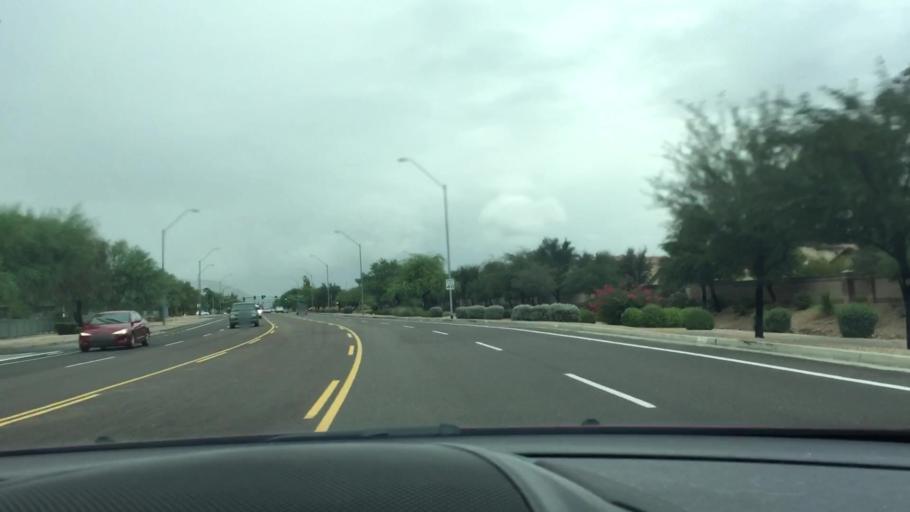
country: US
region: Arizona
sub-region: Maricopa County
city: Sun City
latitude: 33.6751
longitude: -112.2379
